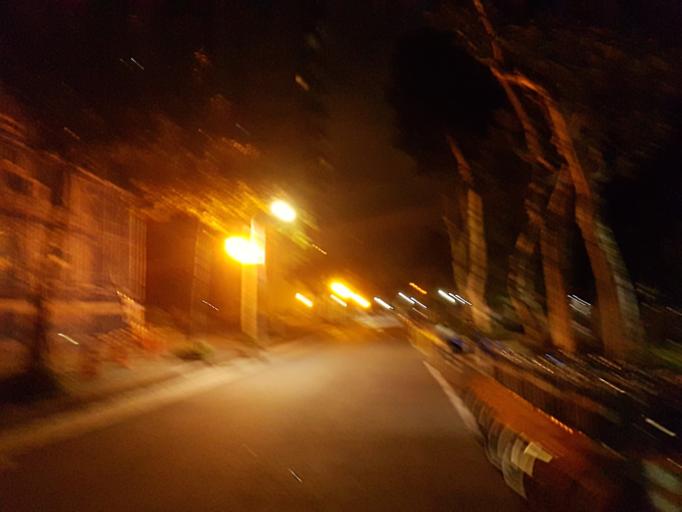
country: TW
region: Taipei
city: Taipei
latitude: 25.0011
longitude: 121.5364
